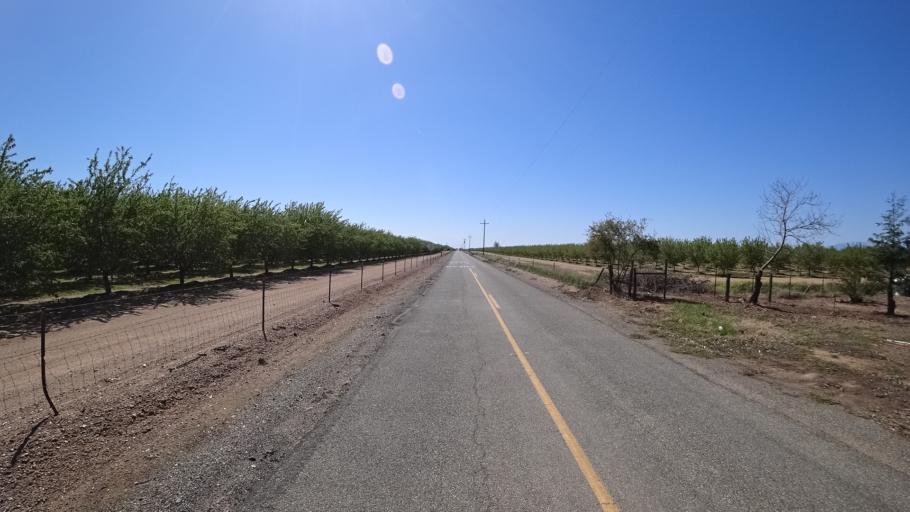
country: US
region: California
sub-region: Glenn County
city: Orland
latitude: 39.6671
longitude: -122.2532
